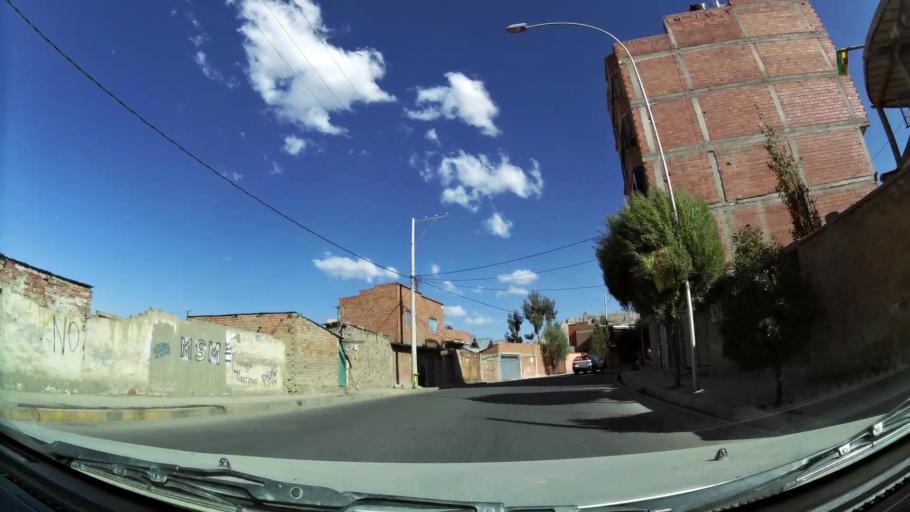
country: BO
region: La Paz
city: La Paz
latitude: -16.5191
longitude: -68.1233
